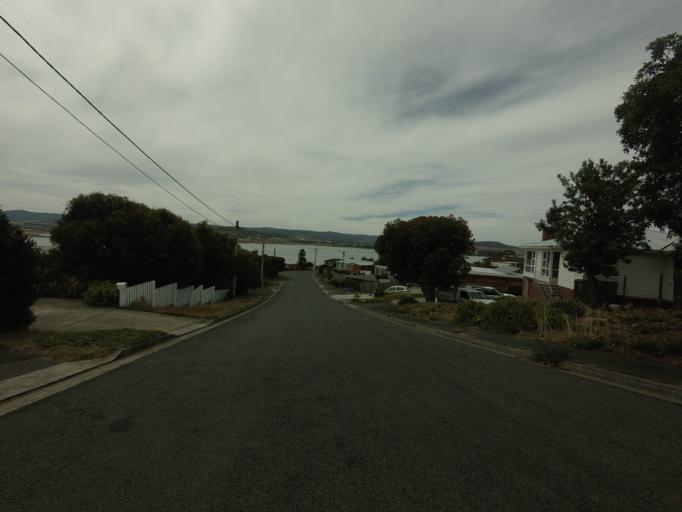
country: AU
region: Tasmania
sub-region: Sorell
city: Sorell
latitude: -42.7940
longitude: 147.5327
